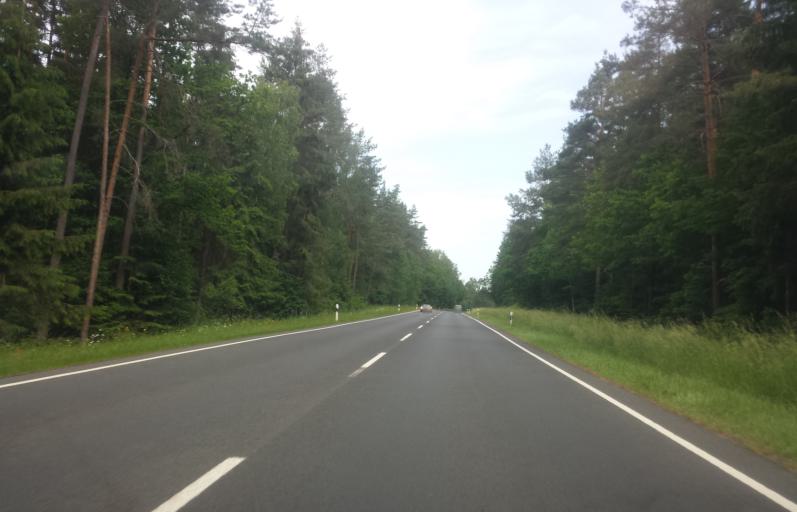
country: DE
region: Bavaria
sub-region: Upper Palatinate
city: Pressath
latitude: 49.7533
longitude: 11.9221
